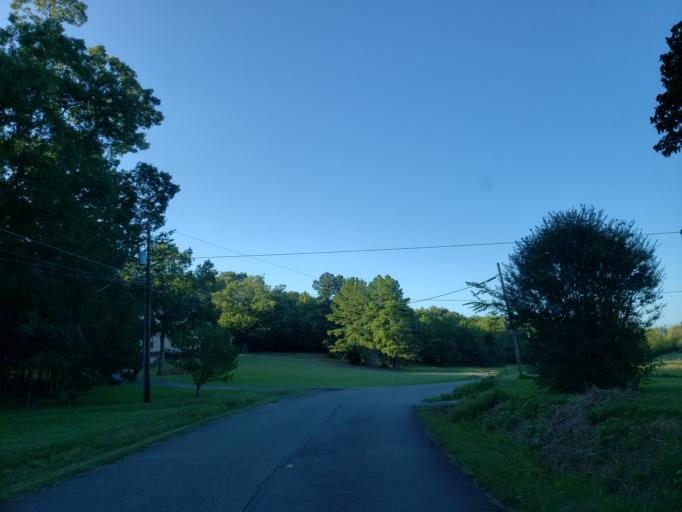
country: US
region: Georgia
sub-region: Bartow County
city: Rydal
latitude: 34.3076
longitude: -84.7332
